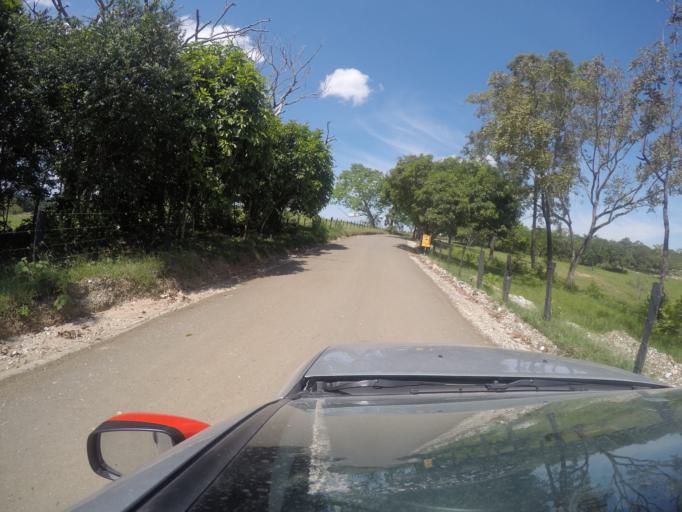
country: CO
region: Antioquia
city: Puerto Triunfo
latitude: 5.9167
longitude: -74.7259
